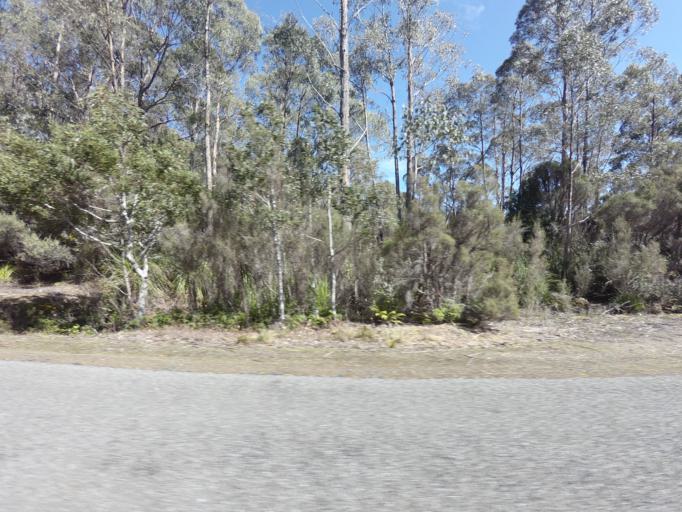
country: AU
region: Tasmania
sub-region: Derwent Valley
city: New Norfolk
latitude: -42.7417
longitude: 146.4183
